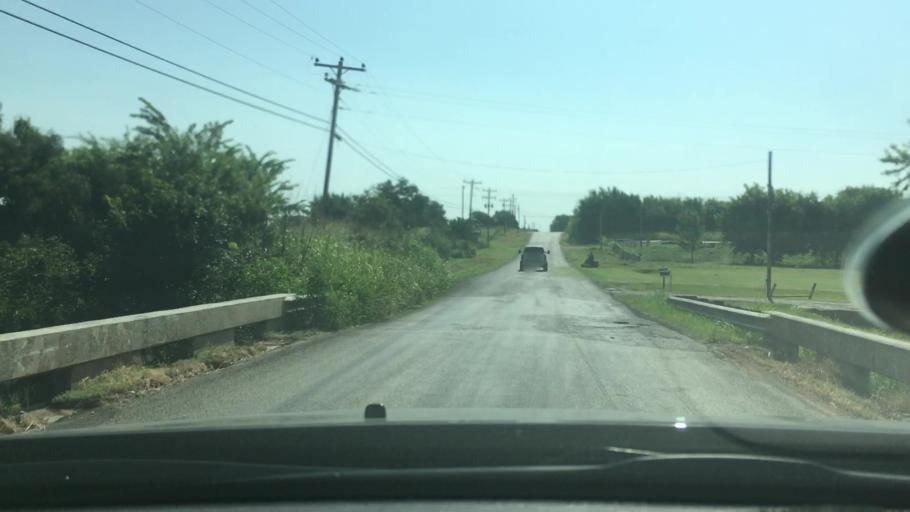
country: US
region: Oklahoma
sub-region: Garvin County
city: Lindsay
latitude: 34.7829
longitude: -97.6013
